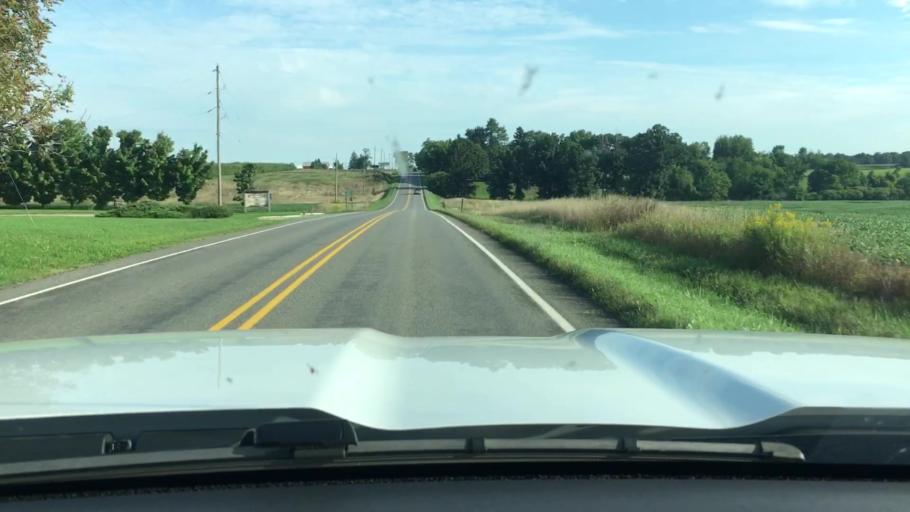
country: US
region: Michigan
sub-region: Kent County
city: Kent City
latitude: 43.1928
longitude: -85.7707
